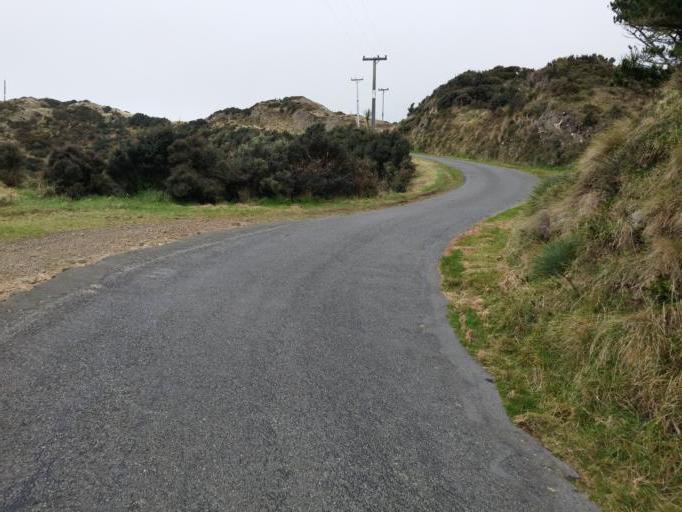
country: NZ
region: Wellington
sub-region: Wellington City
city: Brooklyn
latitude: -41.3234
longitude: 174.7324
